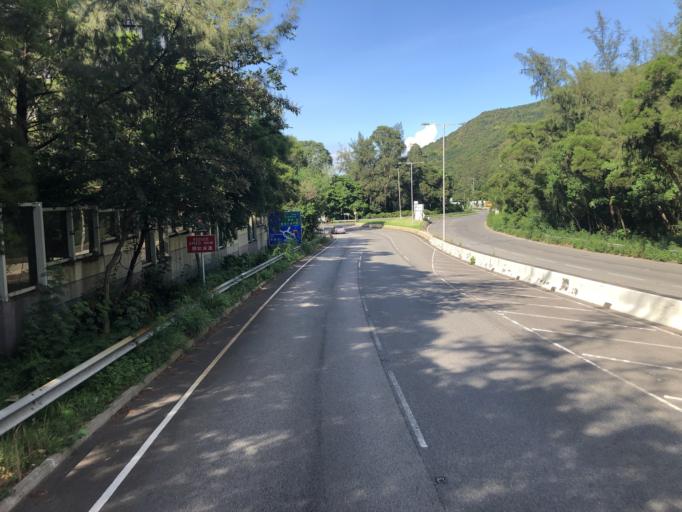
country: HK
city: Tai O
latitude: 22.2884
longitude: 113.9461
